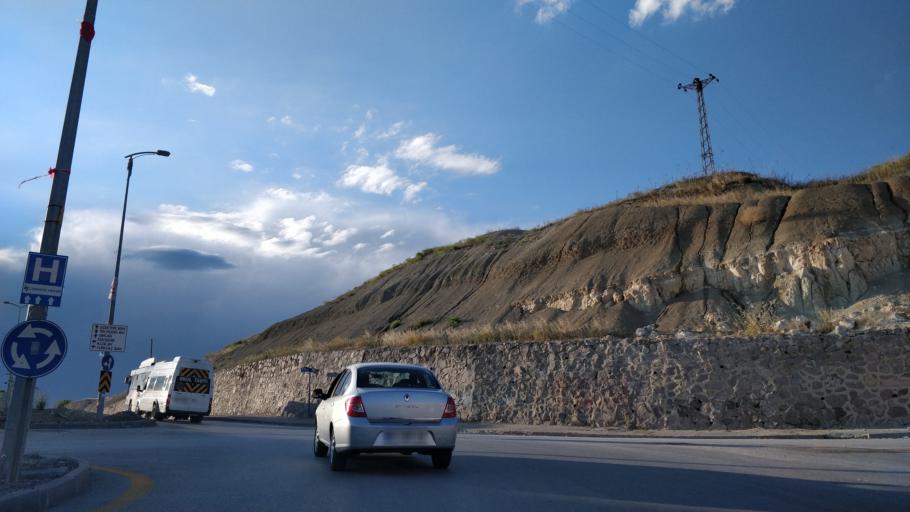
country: TR
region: Ankara
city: Etimesgut
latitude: 39.8317
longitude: 32.5551
